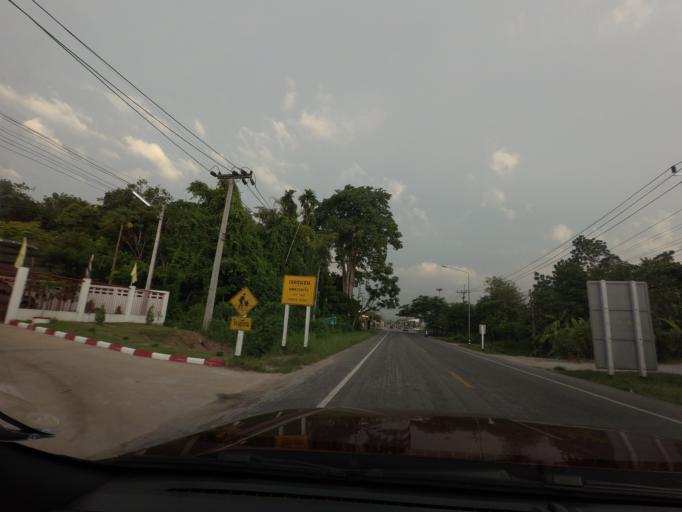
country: TH
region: Pattani
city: Mae Lan
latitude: 6.5840
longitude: 101.1973
